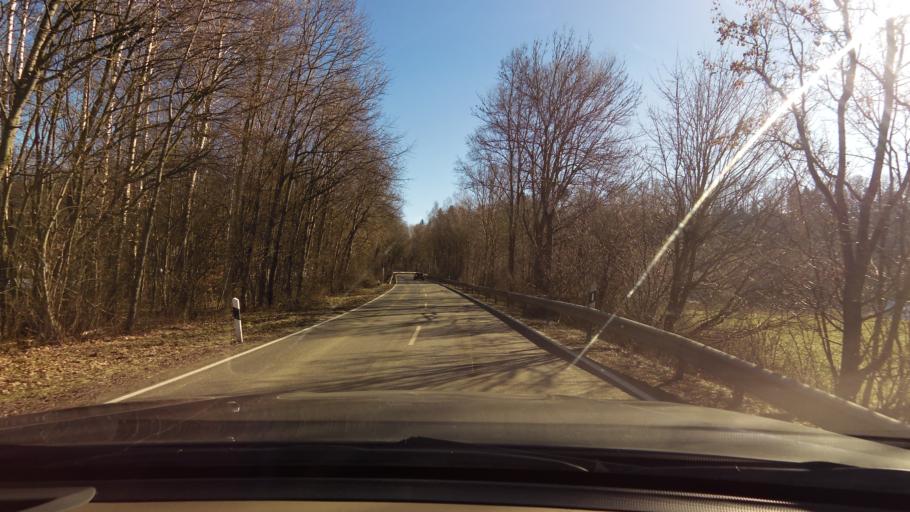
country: DE
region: Bavaria
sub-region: Upper Bavaria
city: Kraiburg am Inn
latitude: 48.1875
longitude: 12.4433
